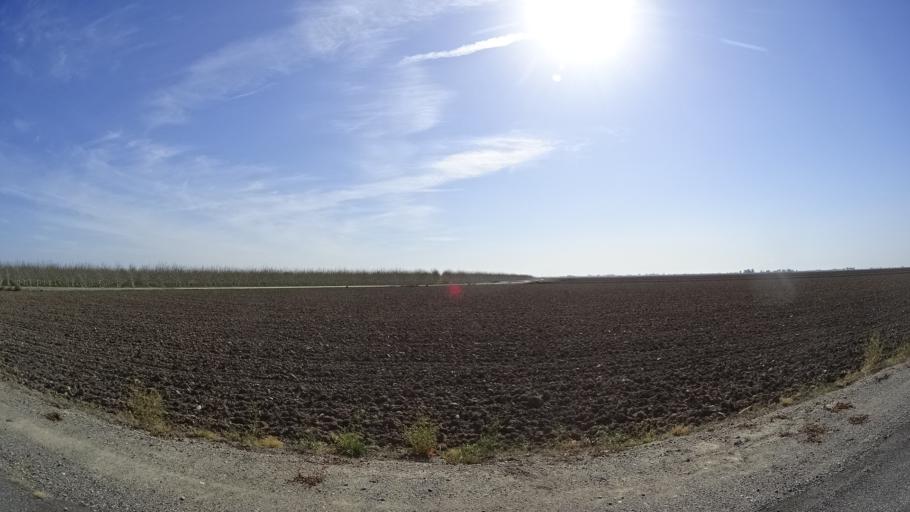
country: US
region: California
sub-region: Glenn County
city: Willows
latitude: 39.6190
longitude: -122.1171
